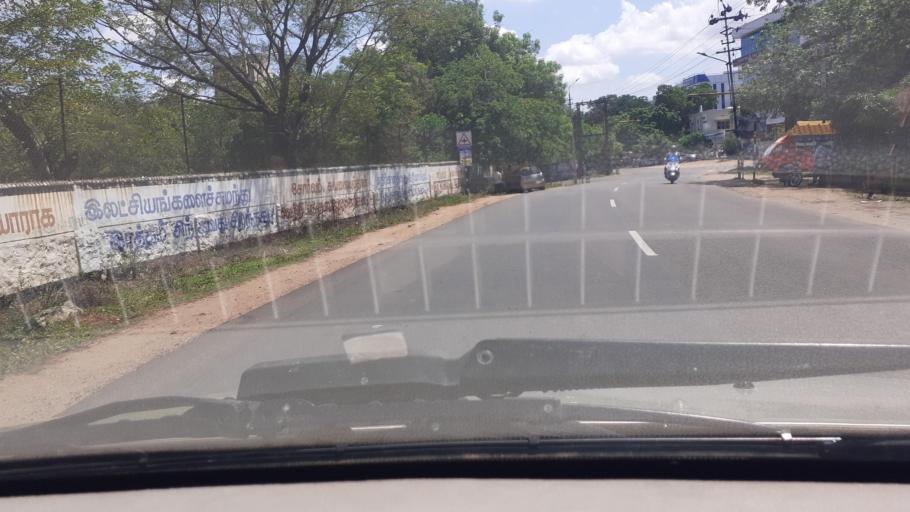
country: IN
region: Tamil Nadu
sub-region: Tirunelveli Kattabo
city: Tirunelveli
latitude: 8.7189
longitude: 77.7403
